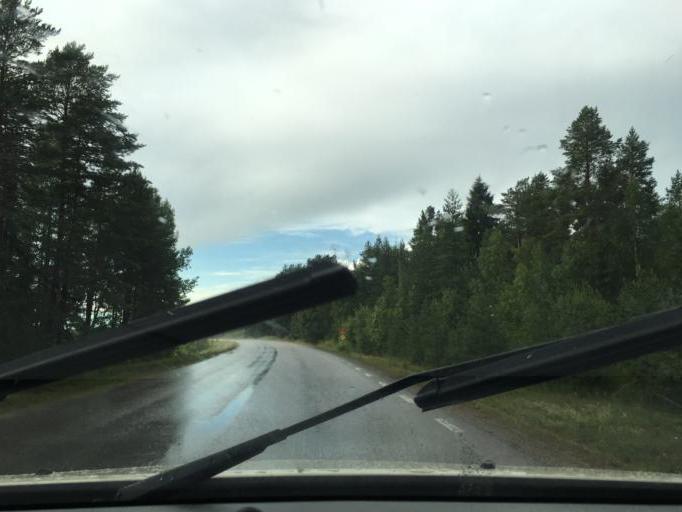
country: SE
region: Norrbotten
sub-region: Kalix Kommun
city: Toere
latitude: 65.9508
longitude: 22.8908
